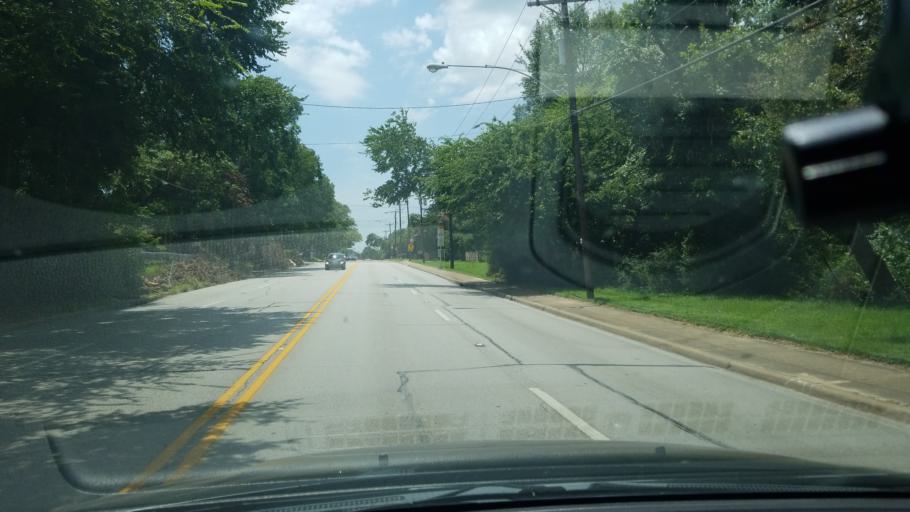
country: US
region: Texas
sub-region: Dallas County
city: Balch Springs
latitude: 32.7147
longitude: -96.6571
